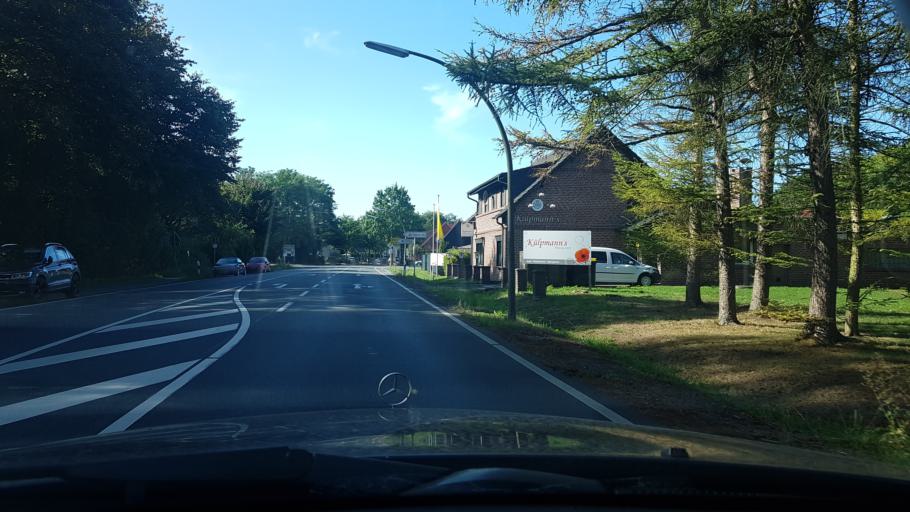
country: DE
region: North Rhine-Westphalia
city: Waltrop
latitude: 51.6002
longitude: 7.3594
